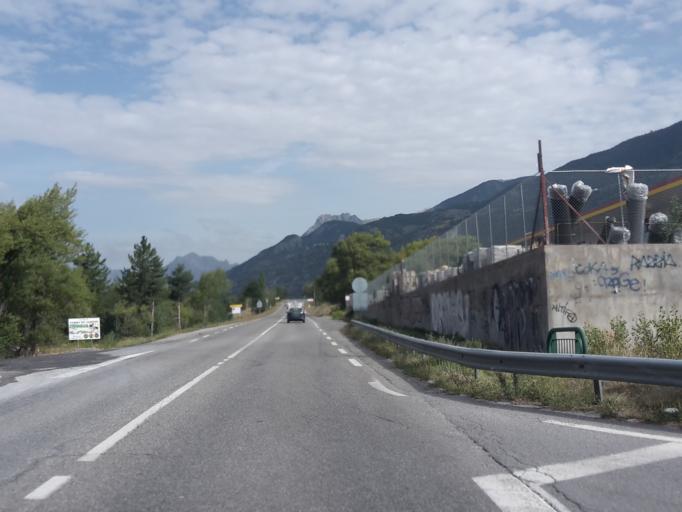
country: FR
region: Provence-Alpes-Cote d'Azur
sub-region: Departement des Hautes-Alpes
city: Guillestre
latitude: 44.6838
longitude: 6.6146
